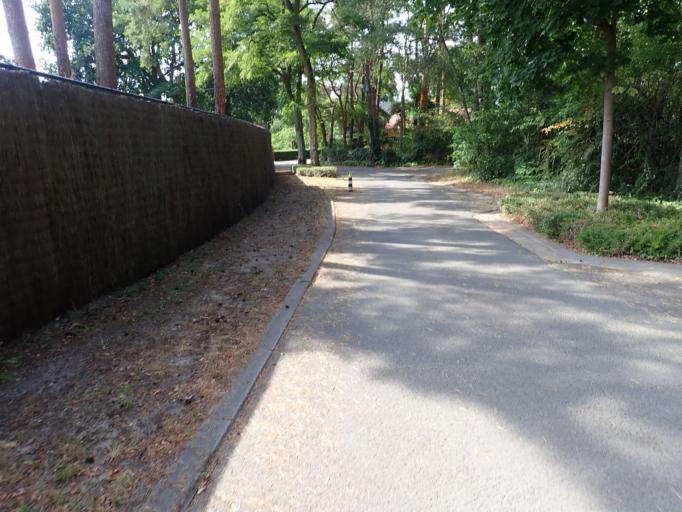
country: BE
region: Flanders
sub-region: Provincie Vlaams-Brabant
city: Keerbergen
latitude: 50.9968
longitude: 4.6351
